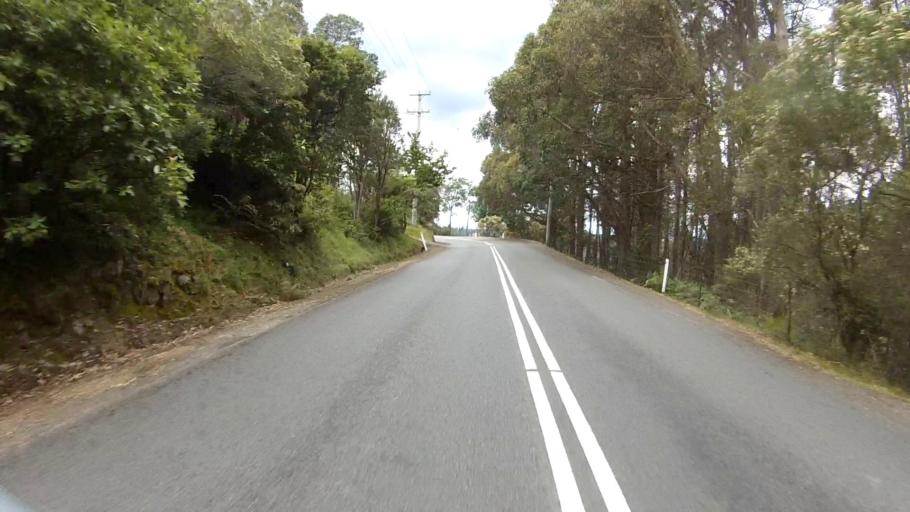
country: AU
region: Tasmania
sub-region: Kingborough
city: Kingston
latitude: -42.9334
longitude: 147.2459
